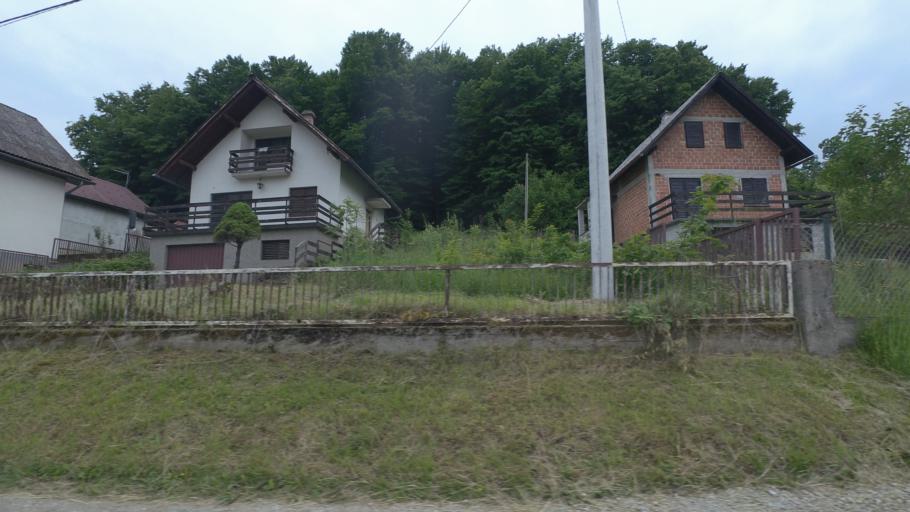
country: HR
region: Karlovacka
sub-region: Grad Karlovac
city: Karlovac
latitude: 45.4217
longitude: 15.5755
